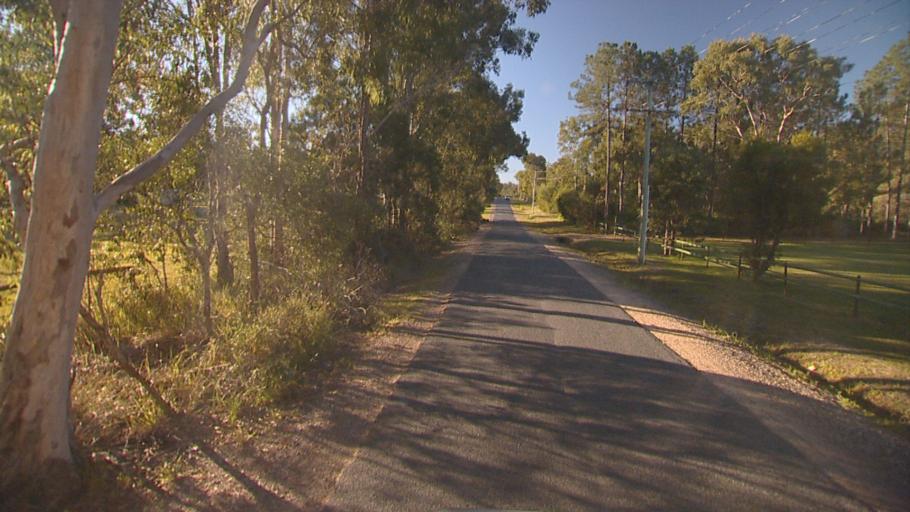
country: AU
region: Queensland
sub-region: Logan
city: Chambers Flat
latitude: -27.7760
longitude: 153.1287
